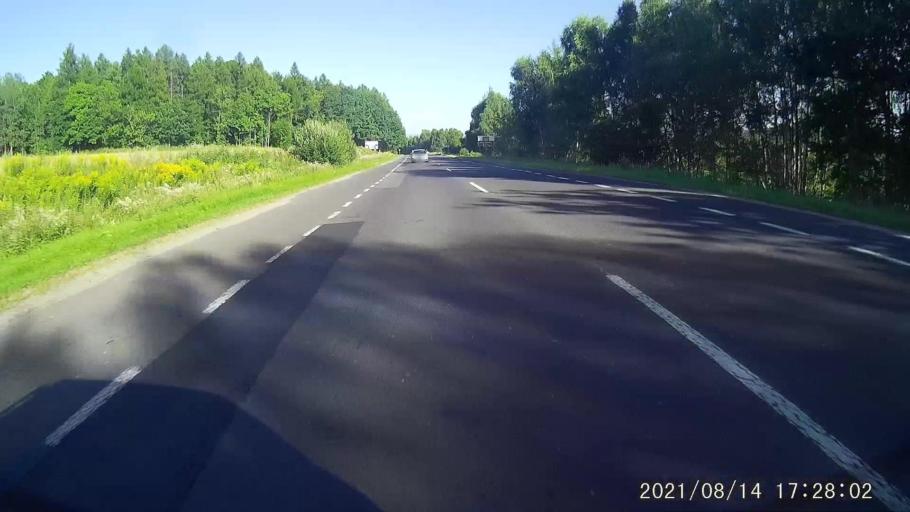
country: PL
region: Lower Silesian Voivodeship
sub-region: Jelenia Gora
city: Jelenia Gora
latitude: 50.9120
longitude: 15.6918
